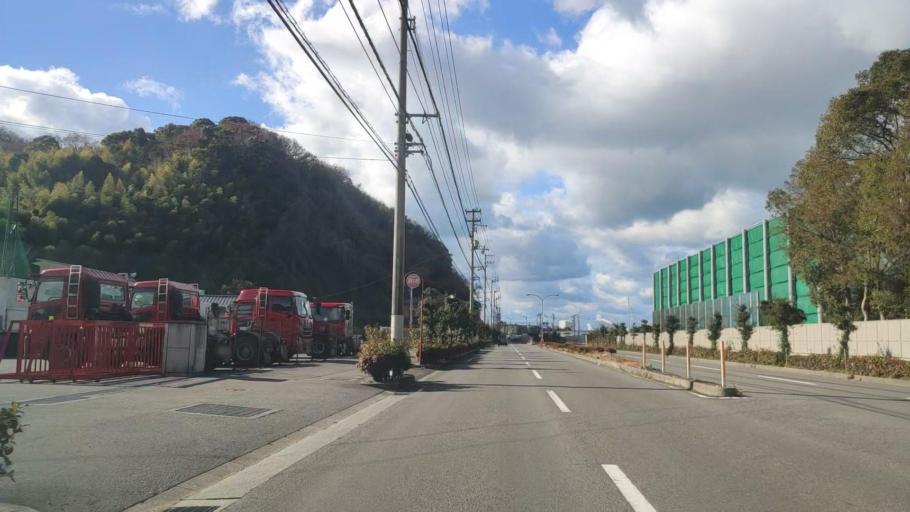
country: JP
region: Ehime
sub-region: Shikoku-chuo Shi
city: Matsuyama
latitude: 33.8475
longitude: 132.7125
